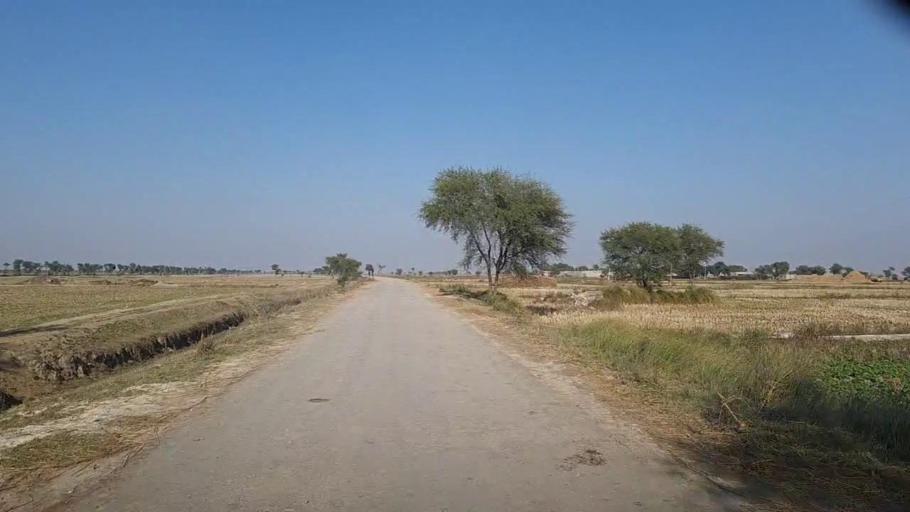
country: PK
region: Sindh
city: Thul
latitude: 28.3530
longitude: 68.7640
